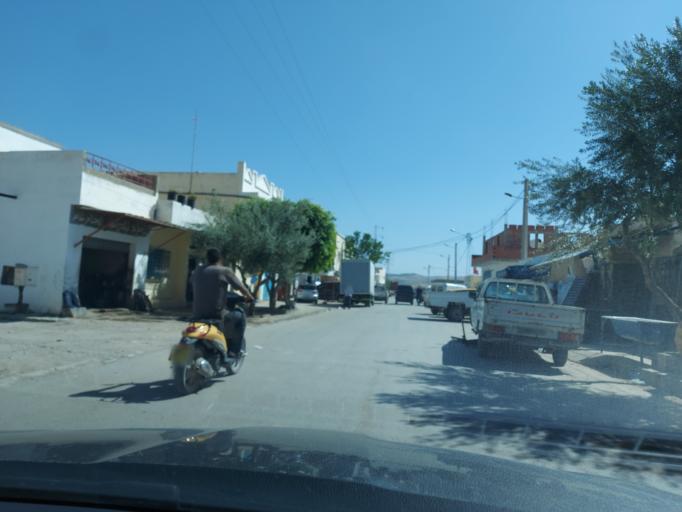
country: TN
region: Silyanah
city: Siliana
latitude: 36.0901
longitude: 9.3763
